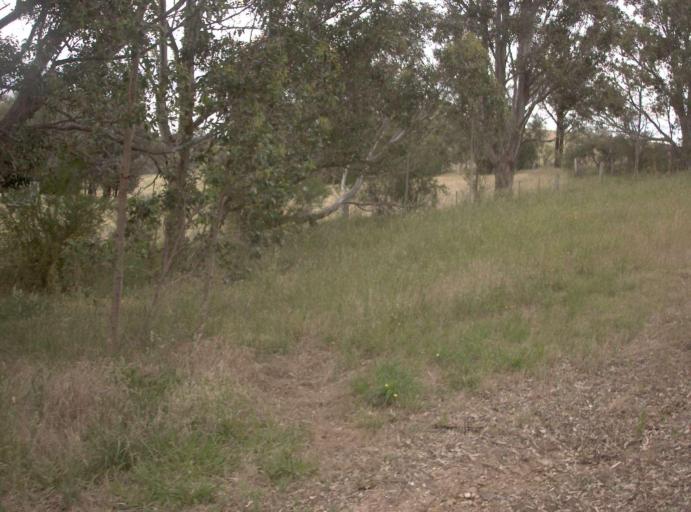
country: AU
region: Victoria
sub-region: East Gippsland
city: Bairnsdale
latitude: -37.7897
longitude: 147.3830
